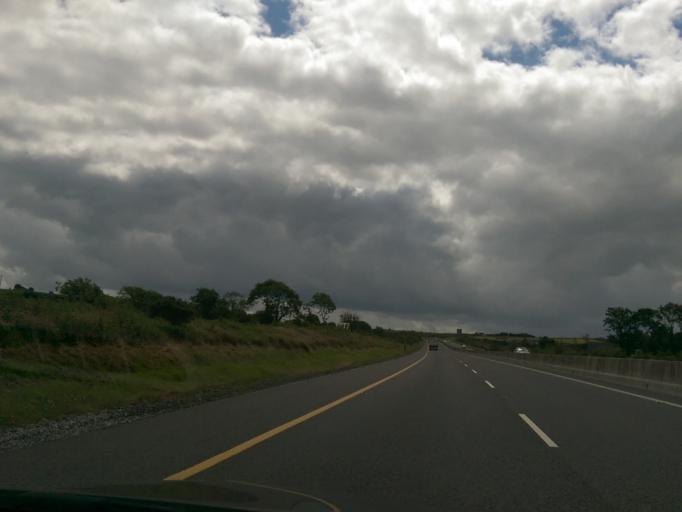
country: IE
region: Munster
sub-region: County Cork
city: Mitchelstown
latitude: 52.2303
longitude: -8.2867
